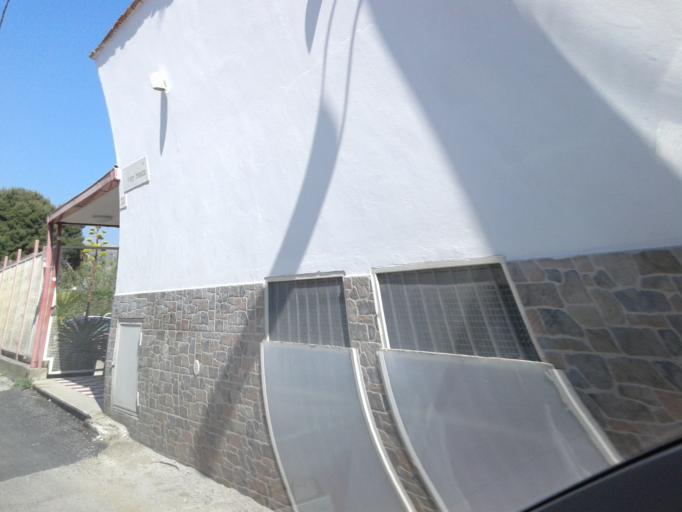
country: IT
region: Sicily
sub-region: Palermo
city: Piano dei Geli
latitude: 38.1098
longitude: 13.3005
